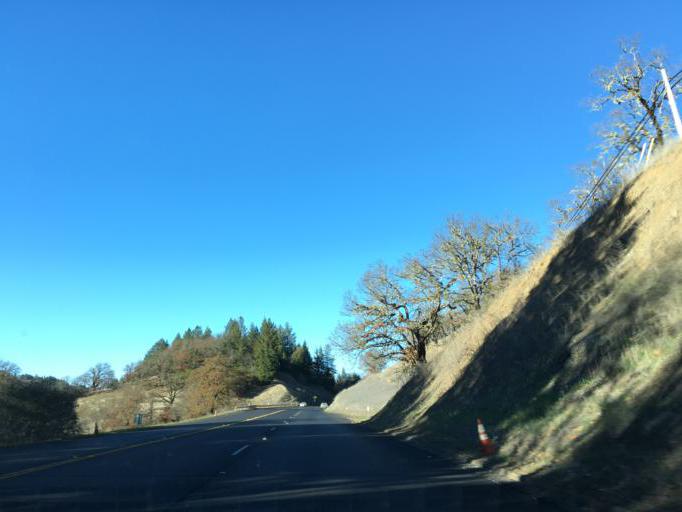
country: US
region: California
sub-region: Mendocino County
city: Laytonville
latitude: 39.7528
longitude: -123.5358
